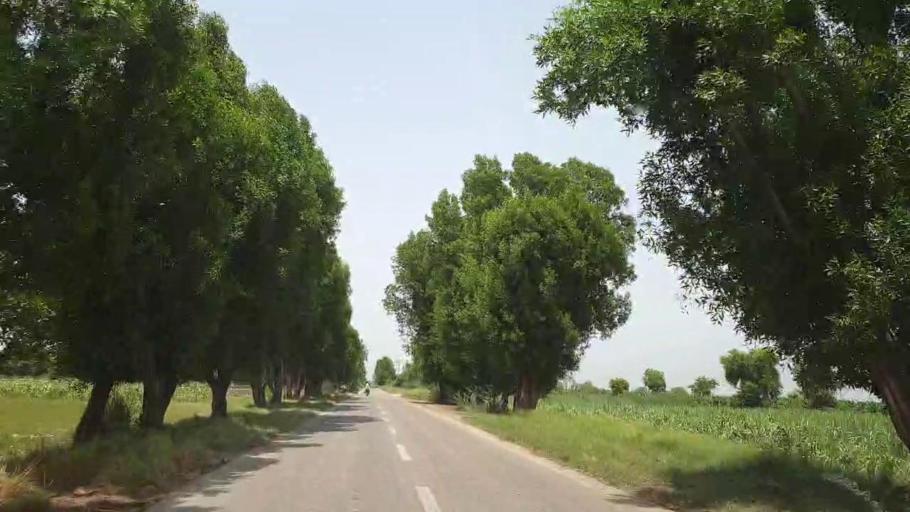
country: PK
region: Sindh
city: Sakrand
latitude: 26.1891
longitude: 68.2342
